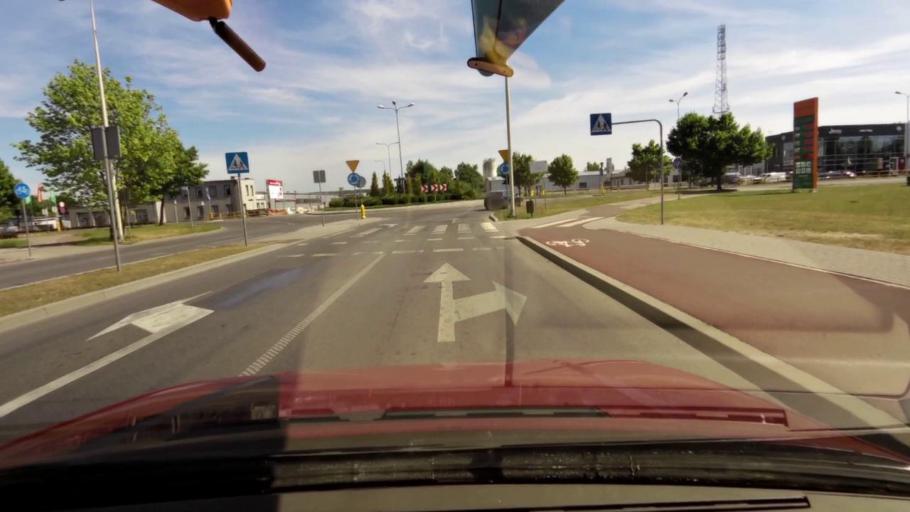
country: PL
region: Pomeranian Voivodeship
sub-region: Slupsk
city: Slupsk
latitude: 54.4528
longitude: 17.0168
